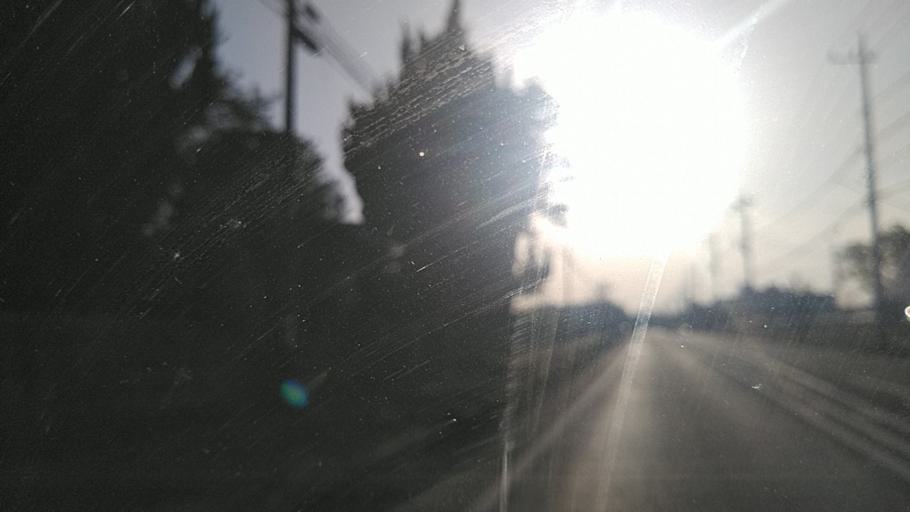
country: JP
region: Gunma
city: Ota
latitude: 36.2757
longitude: 139.3475
